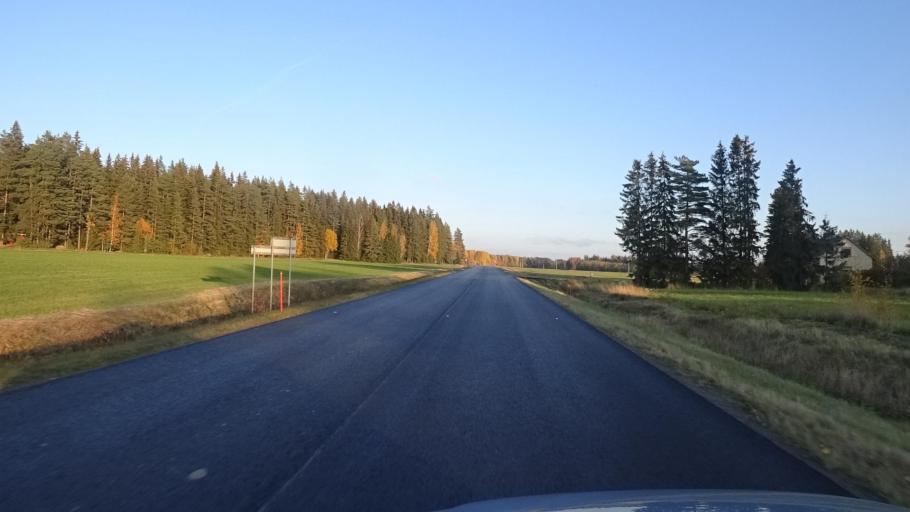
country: FI
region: Haeme
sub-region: Forssa
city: Ypaejae
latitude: 60.7772
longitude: 23.3172
